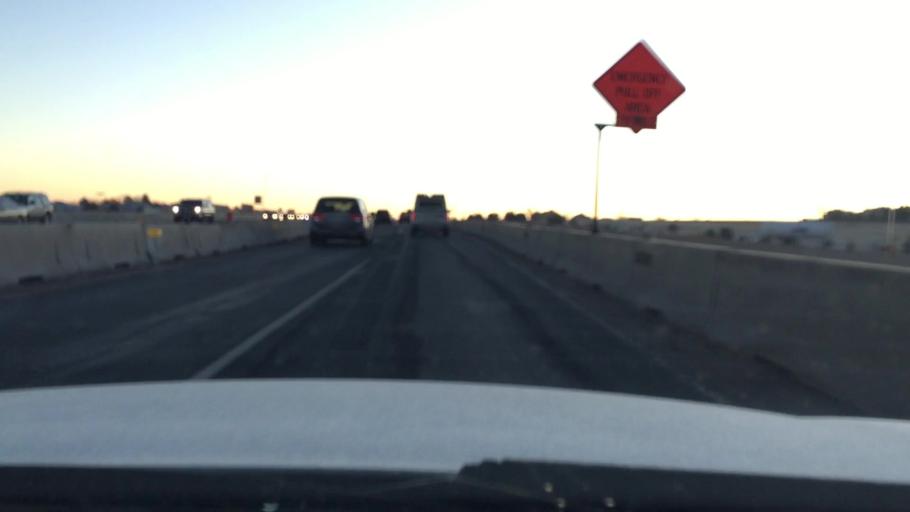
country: US
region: Colorado
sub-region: Douglas County
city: Highlands Ranch
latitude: 39.5632
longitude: -104.9599
